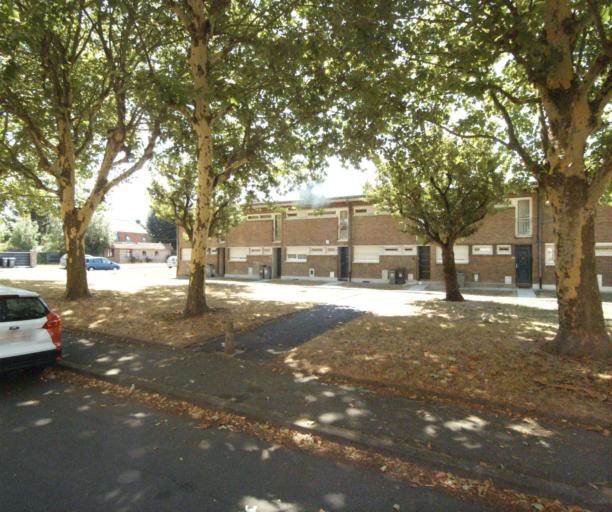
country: FR
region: Nord-Pas-de-Calais
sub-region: Departement du Nord
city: Wattrelos
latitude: 50.7073
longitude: 3.2285
